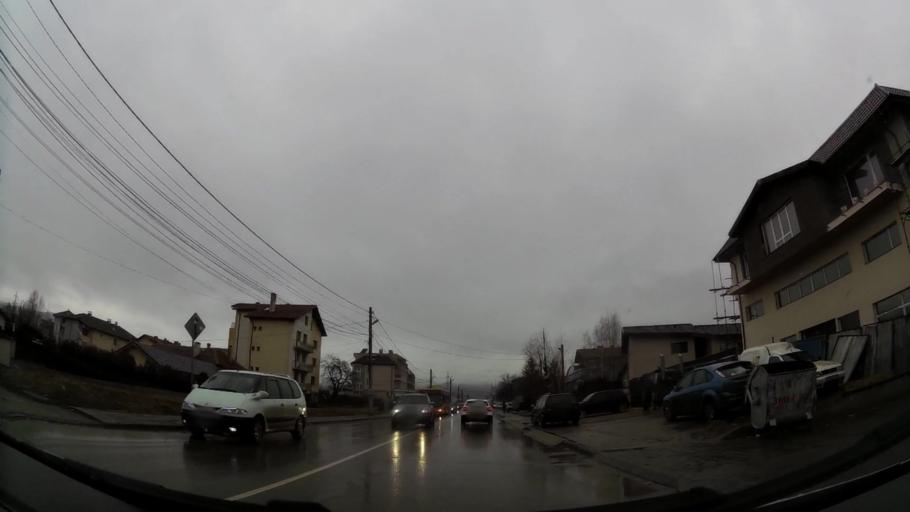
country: BG
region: Sofia-Capital
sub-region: Stolichna Obshtina
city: Sofia
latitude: 42.6247
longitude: 23.4061
